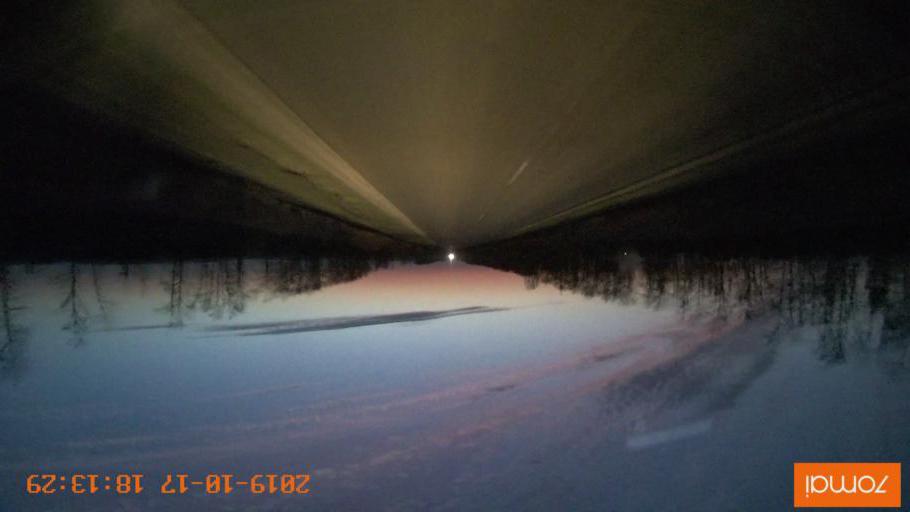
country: RU
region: Tula
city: Kurkino
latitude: 53.4096
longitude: 38.5866
